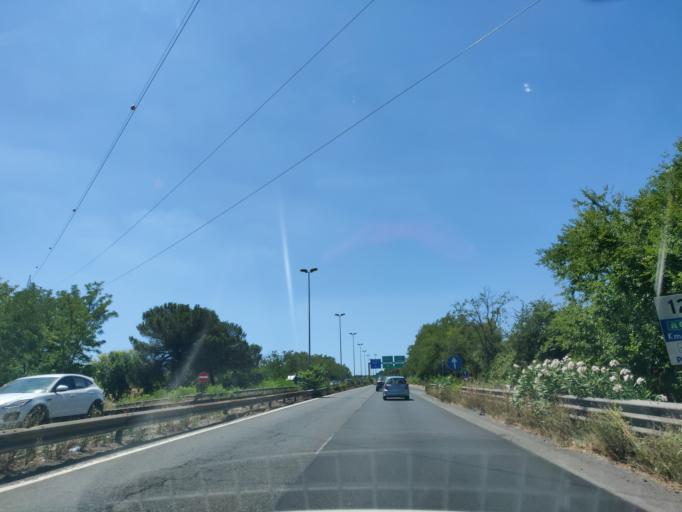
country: IT
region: Latium
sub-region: Citta metropolitana di Roma Capitale
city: Selcetta
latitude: 41.8068
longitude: 12.4561
